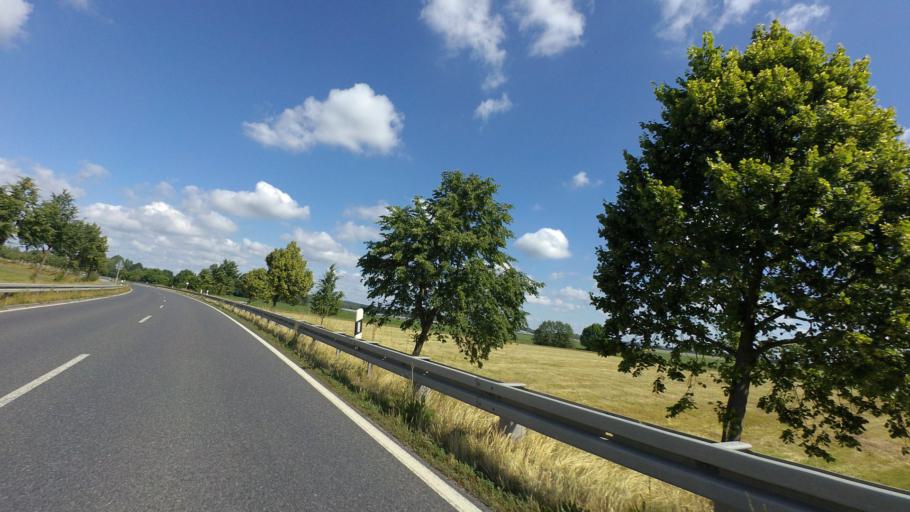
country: DE
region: Saxony
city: Kamenz
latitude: 51.2861
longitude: 14.1276
